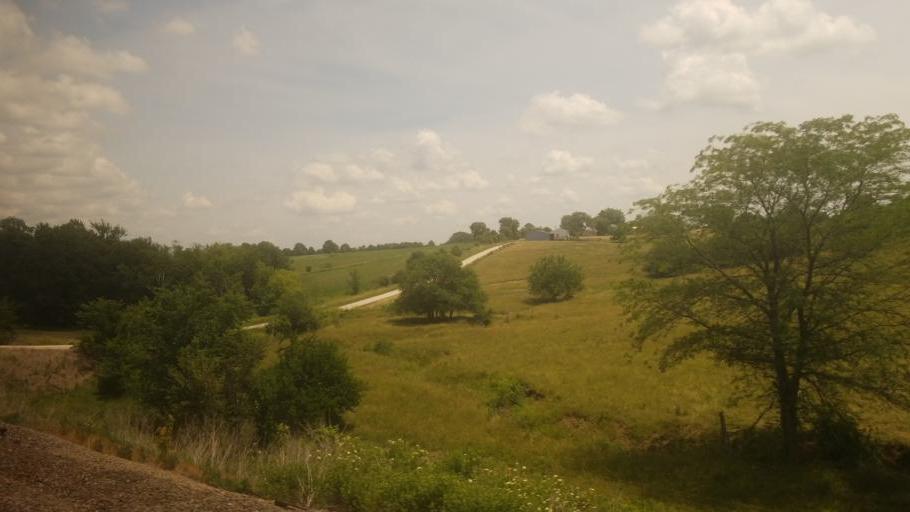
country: US
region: Missouri
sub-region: Macon County
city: La Plata
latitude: 40.0509
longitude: -92.4678
